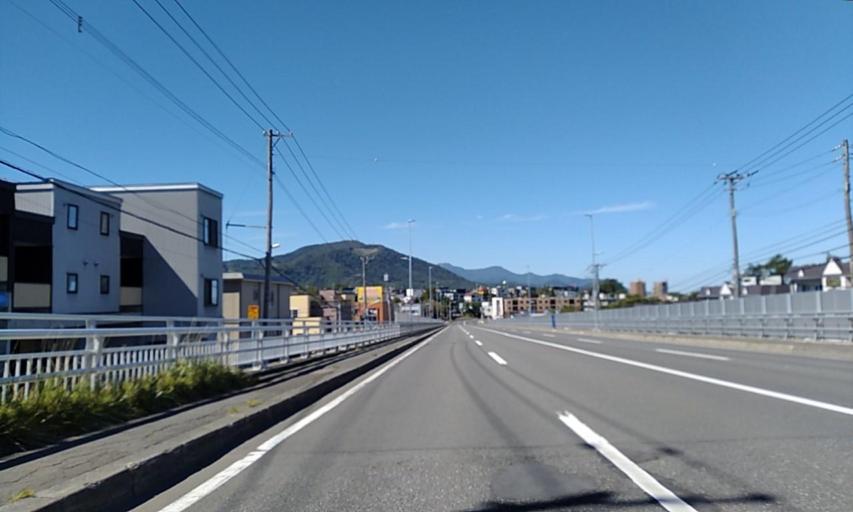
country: JP
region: Hokkaido
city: Sapporo
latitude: 43.0088
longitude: 141.3780
